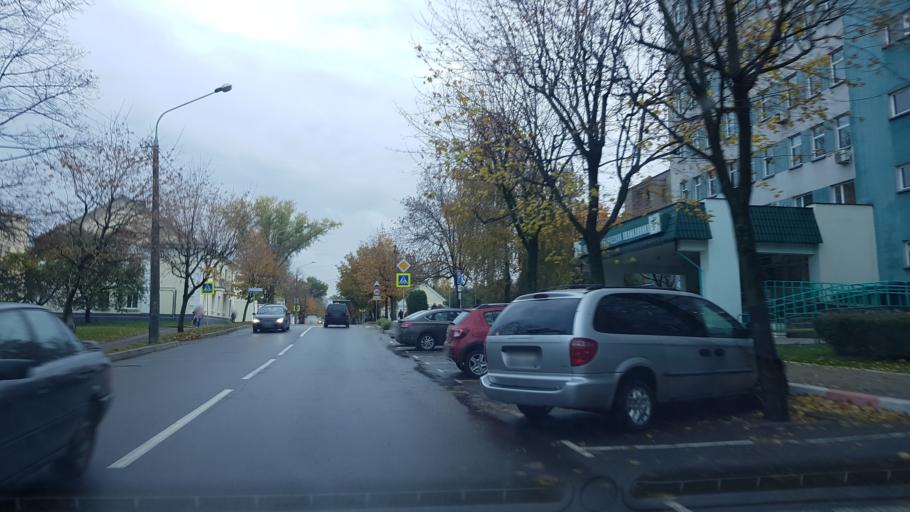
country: BY
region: Minsk
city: Syenitsa
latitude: 53.8481
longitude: 27.5503
